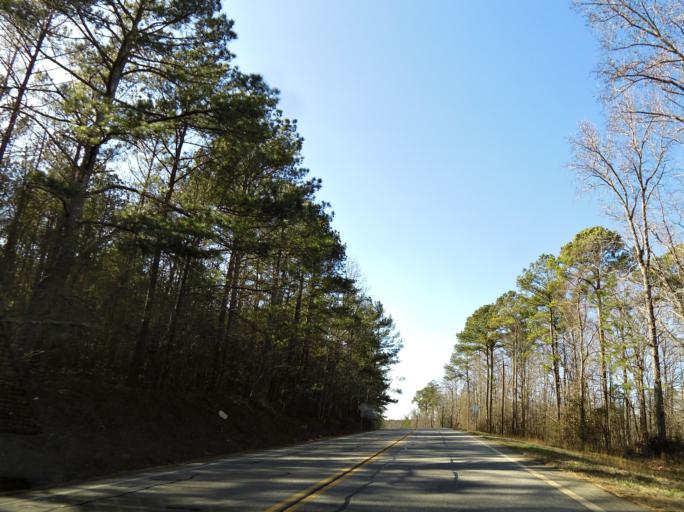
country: US
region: Georgia
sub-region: Lamar County
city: Barnesville
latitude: 32.9188
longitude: -84.1779
